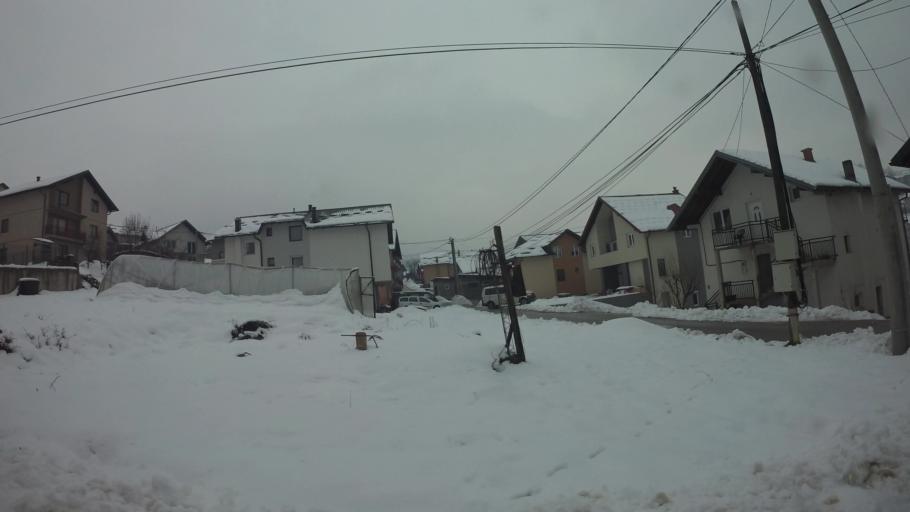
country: BA
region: Federation of Bosnia and Herzegovina
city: Hadzici
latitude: 43.8456
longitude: 18.2618
